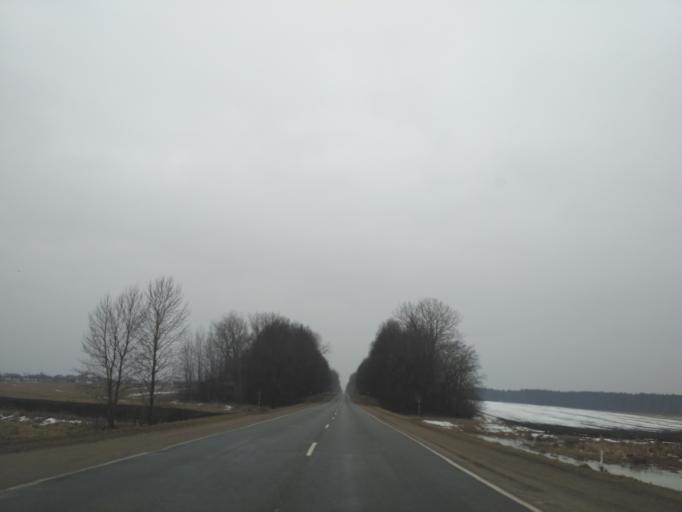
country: BY
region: Minsk
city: Haradzyeya
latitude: 53.3722
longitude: 26.5390
